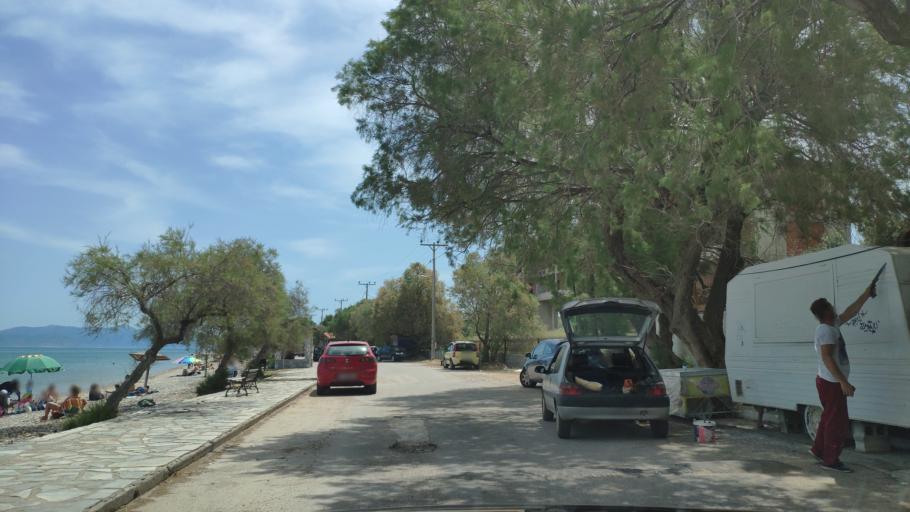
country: GR
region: Attica
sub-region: Nomarchia Anatolikis Attikis
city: Grammatiko
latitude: 38.2632
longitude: 23.9764
